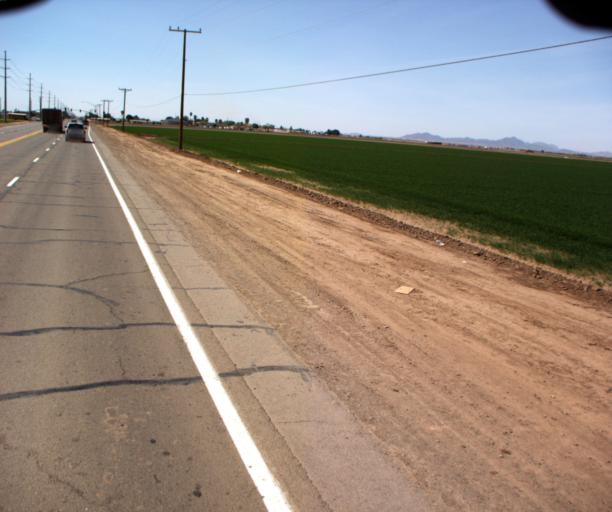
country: US
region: Arizona
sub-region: Yuma County
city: Yuma
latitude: 32.6993
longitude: -114.5181
